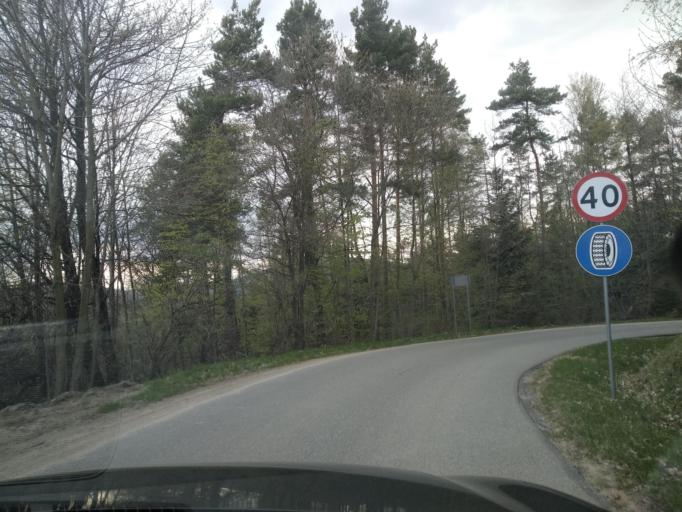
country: PL
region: Subcarpathian Voivodeship
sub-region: Powiat leski
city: Baligrod
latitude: 49.3578
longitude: 22.2265
